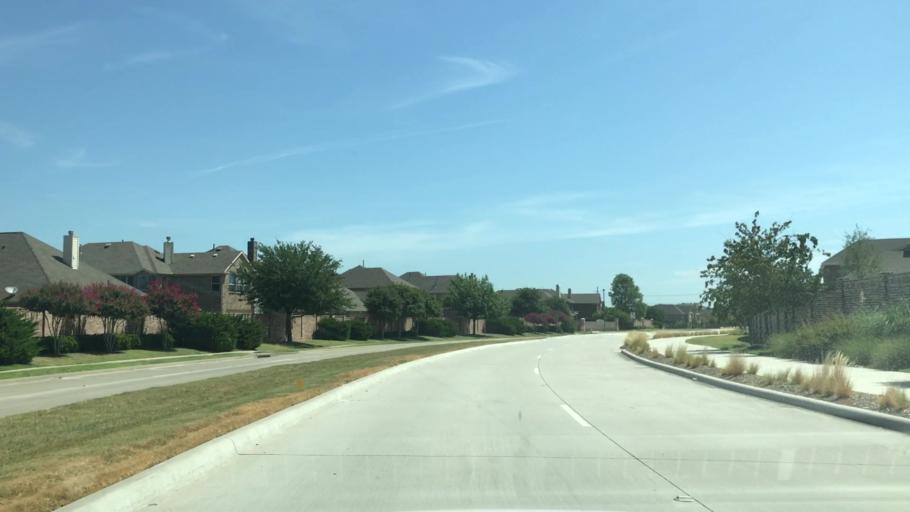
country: US
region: Texas
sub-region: Collin County
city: Allen
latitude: 33.1222
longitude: -96.6742
